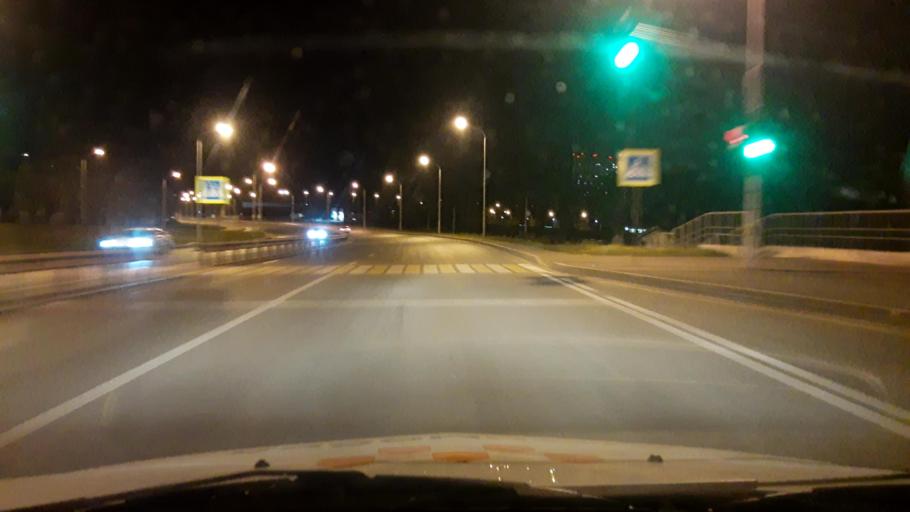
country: RU
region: Bashkortostan
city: Ufa
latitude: 54.8001
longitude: 56.1272
